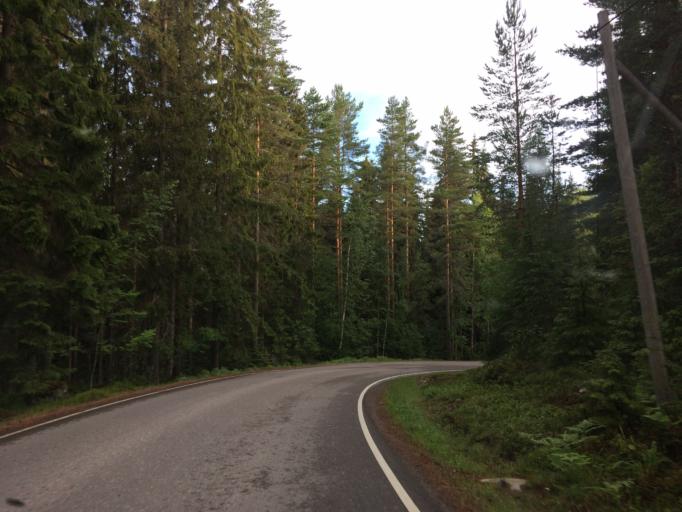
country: FI
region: Haeme
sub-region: Haemeenlinna
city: Janakkala
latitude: 60.8629
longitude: 24.5501
